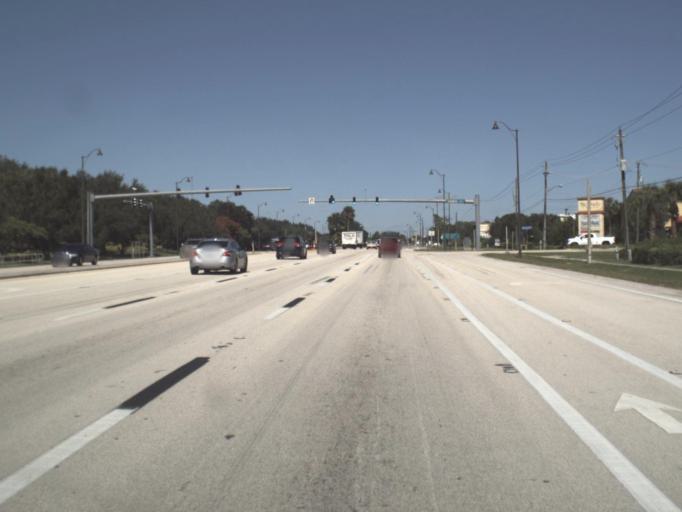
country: US
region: Florida
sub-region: Lee County
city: Bonita Springs
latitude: 26.3697
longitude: -81.8077
